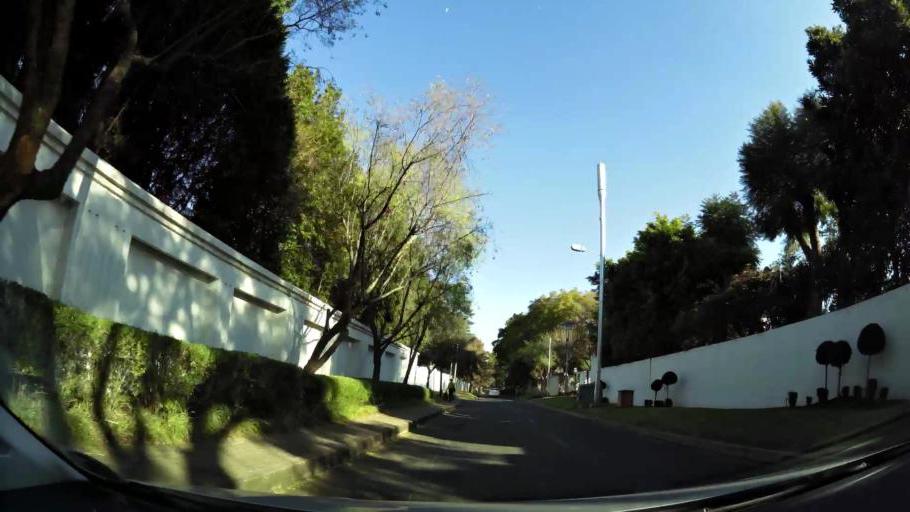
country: ZA
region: Gauteng
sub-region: City of Johannesburg Metropolitan Municipality
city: Johannesburg
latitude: -26.1104
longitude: 28.0660
